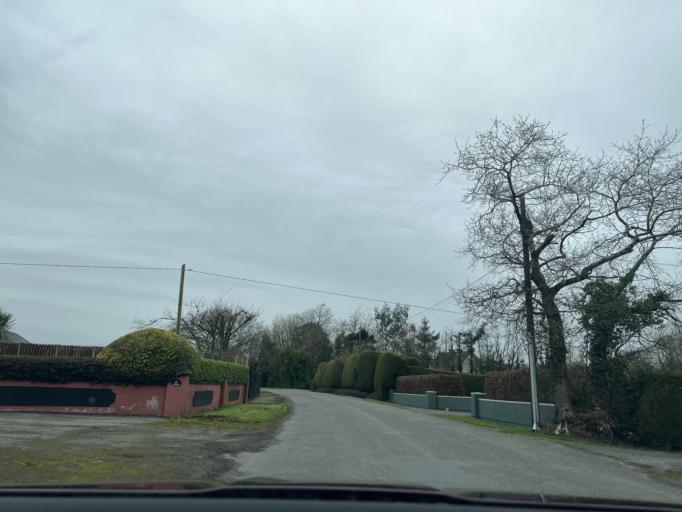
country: IE
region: Leinster
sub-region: Loch Garman
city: Castlebridge
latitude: 52.3833
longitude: -6.5288
